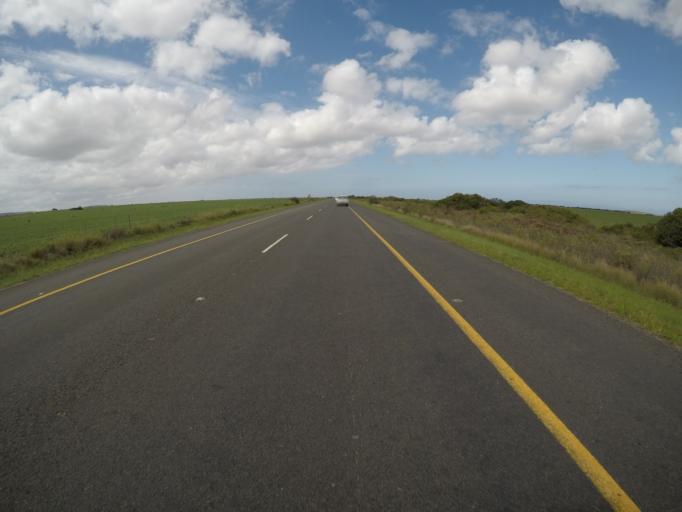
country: ZA
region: Western Cape
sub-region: Eden District Municipality
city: Mossel Bay
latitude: -34.1784
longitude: 21.9378
